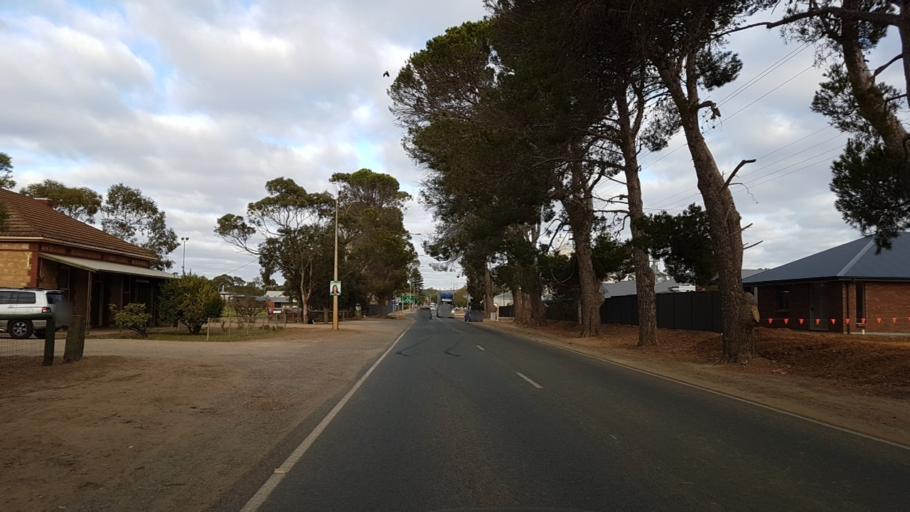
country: AU
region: South Australia
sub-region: Alexandrina
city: Strathalbyn
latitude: -35.2564
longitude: 138.9031
